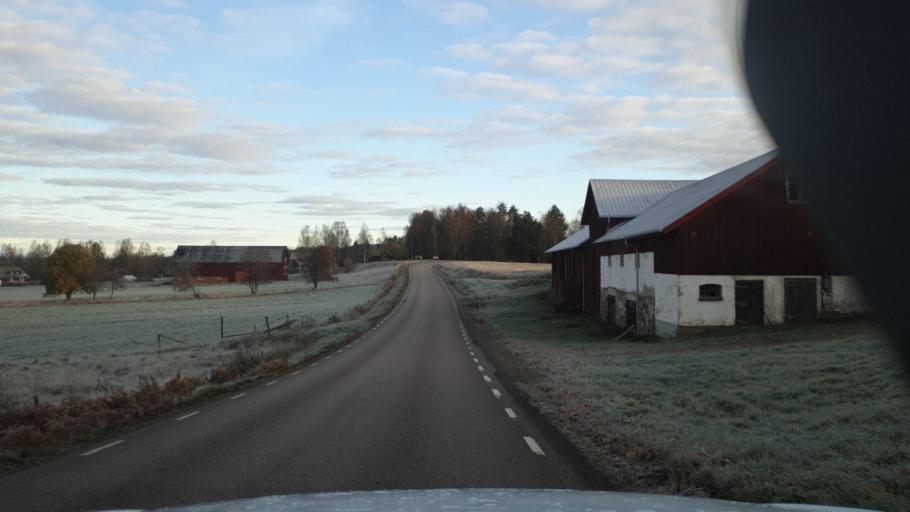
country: SE
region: Vaermland
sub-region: Eda Kommun
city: Charlottenberg
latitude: 59.7775
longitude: 12.2108
